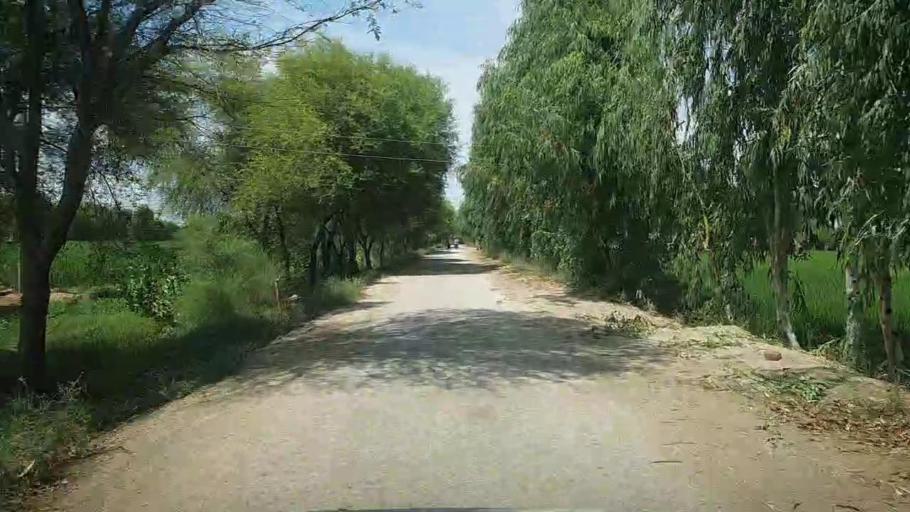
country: PK
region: Sindh
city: Kandhkot
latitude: 28.2973
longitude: 69.2363
